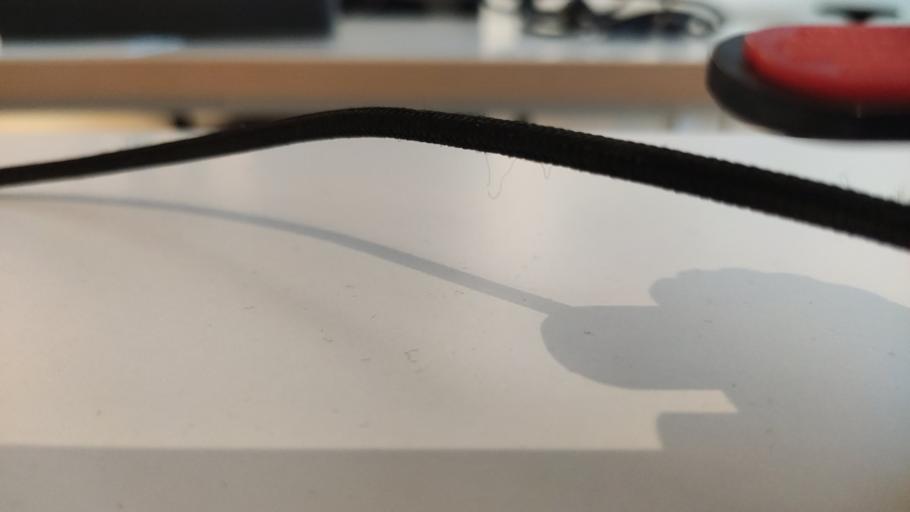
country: RU
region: Moskovskaya
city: Novopetrovskoye
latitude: 55.9198
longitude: 36.4380
